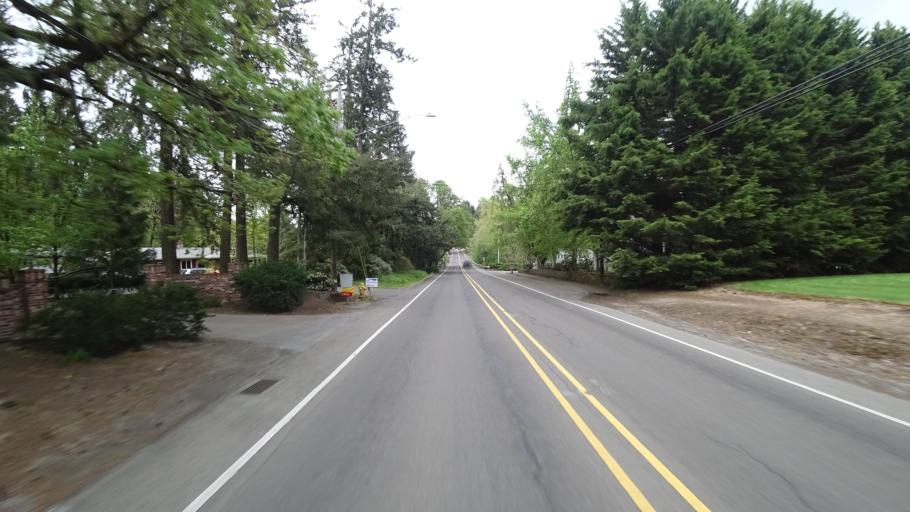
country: US
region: Oregon
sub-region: Washington County
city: Hillsboro
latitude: 45.5477
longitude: -122.9797
